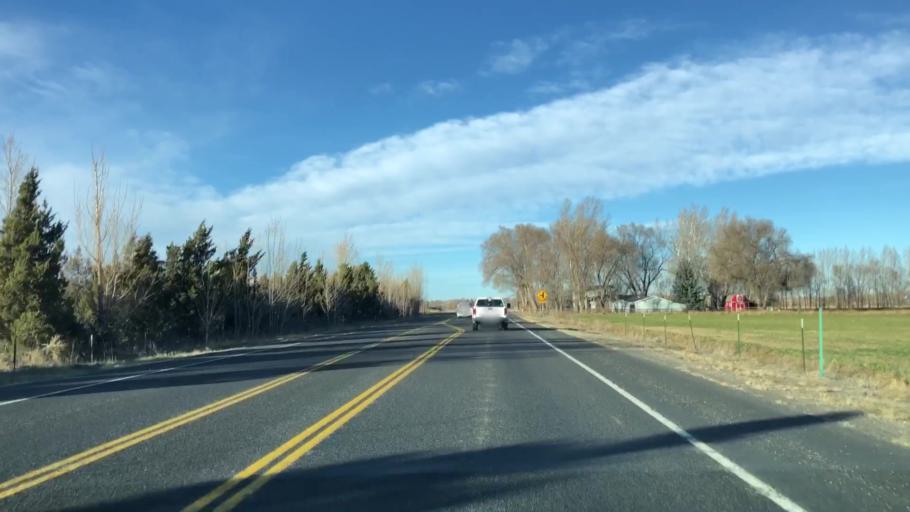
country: US
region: Colorado
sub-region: Weld County
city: Windsor
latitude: 40.5065
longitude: -104.9818
